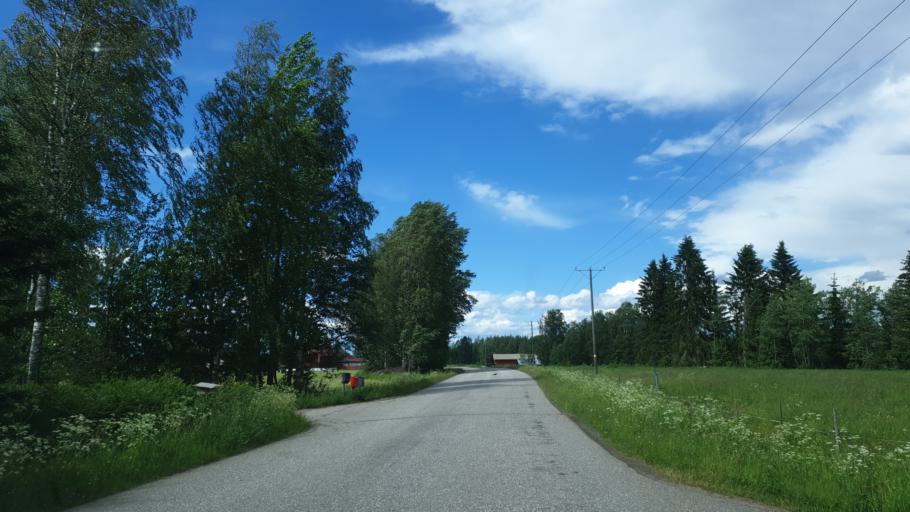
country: FI
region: Northern Savo
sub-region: Koillis-Savo
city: Kaavi
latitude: 62.9884
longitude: 28.7308
